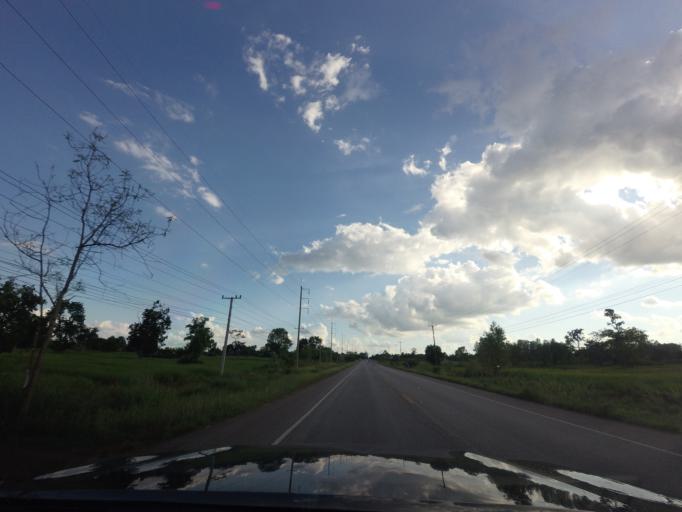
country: TH
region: Changwat Udon Thani
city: Thung Fon
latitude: 17.4614
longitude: 103.1895
